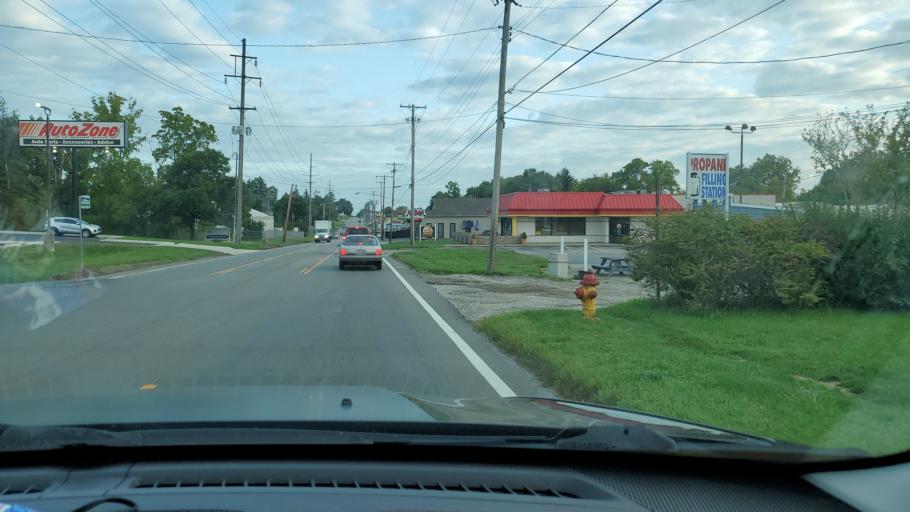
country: US
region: Ohio
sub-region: Mahoning County
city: Struthers
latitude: 41.0518
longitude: -80.6158
